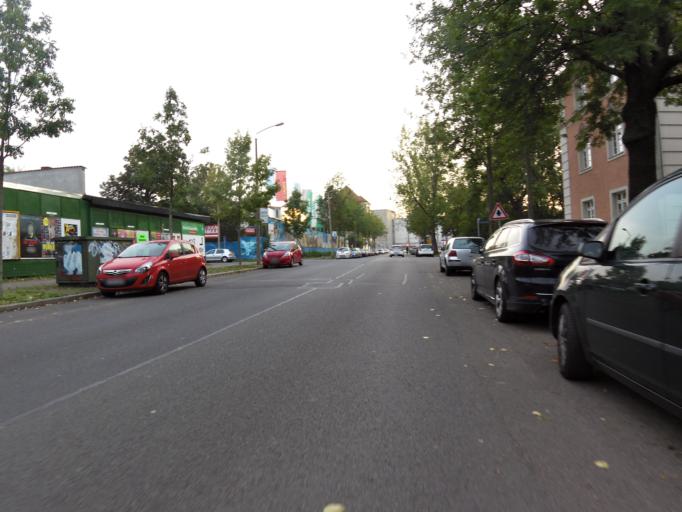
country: DE
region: Saxony
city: Leipzig
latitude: 51.3234
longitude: 12.4052
